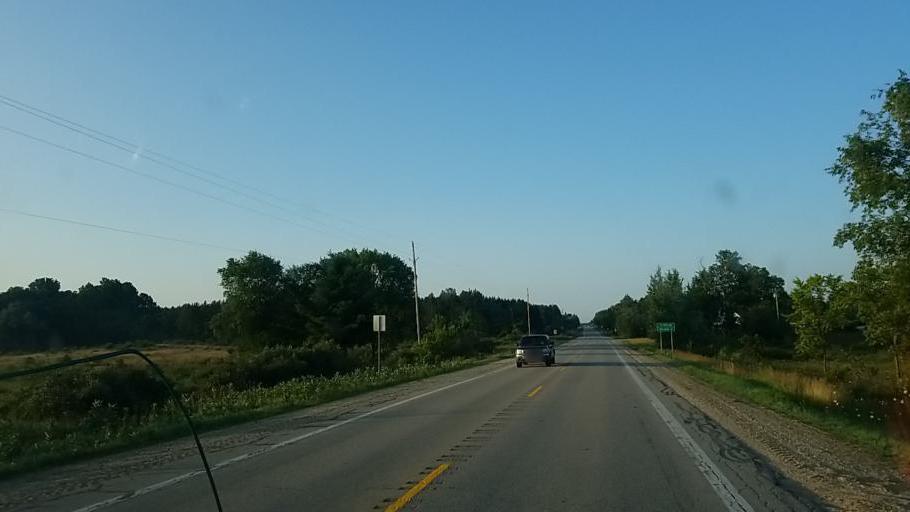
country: US
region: Michigan
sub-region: Isabella County
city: Lake Isabella
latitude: 43.6273
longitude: -85.1461
